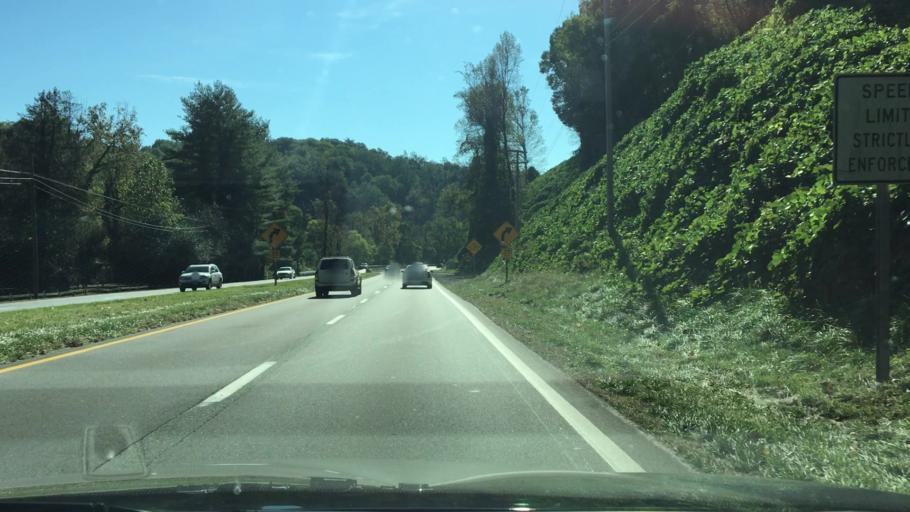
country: US
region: Virginia
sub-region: Roanoke County
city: Narrows
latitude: 37.1235
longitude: -79.9579
